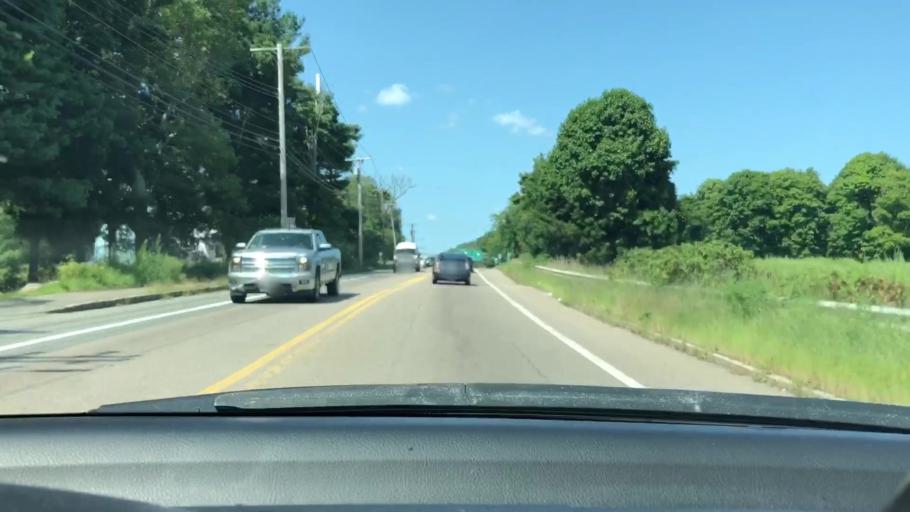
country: US
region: Massachusetts
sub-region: Norfolk County
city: Canton
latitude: 42.1976
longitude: -71.1191
